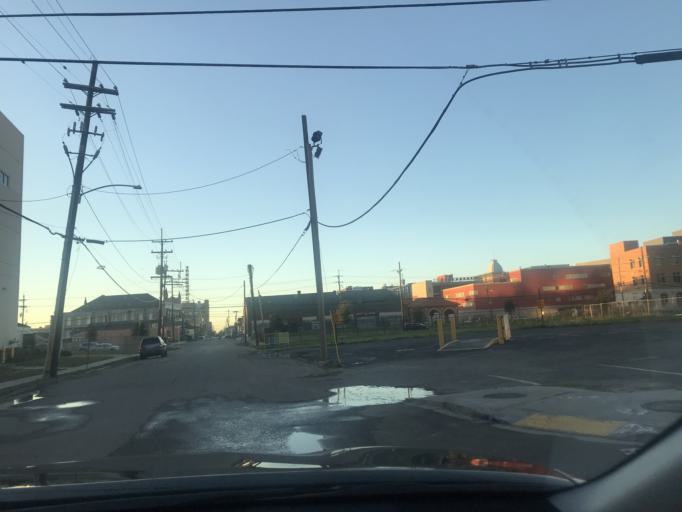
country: US
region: Louisiana
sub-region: Orleans Parish
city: New Orleans
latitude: 29.9577
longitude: -90.0848
